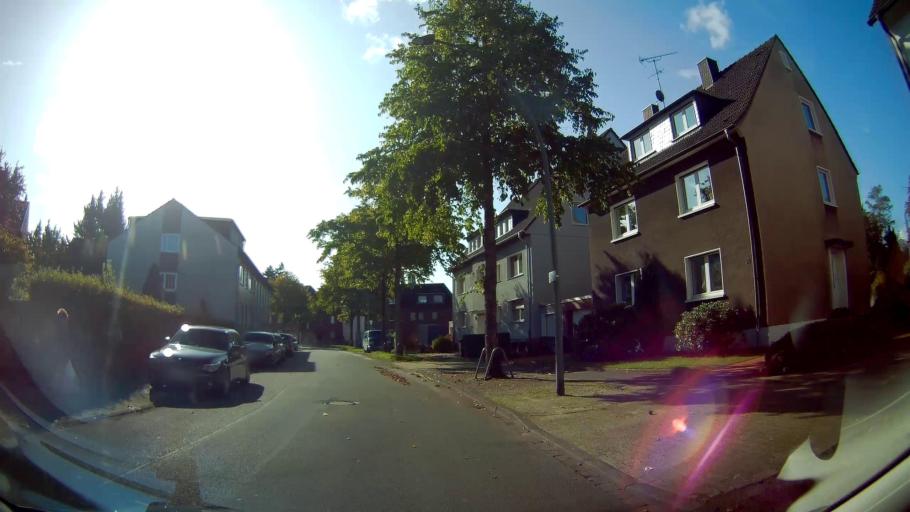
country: DE
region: North Rhine-Westphalia
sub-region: Regierungsbezirk Munster
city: Bottrop
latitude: 51.5182
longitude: 6.9394
